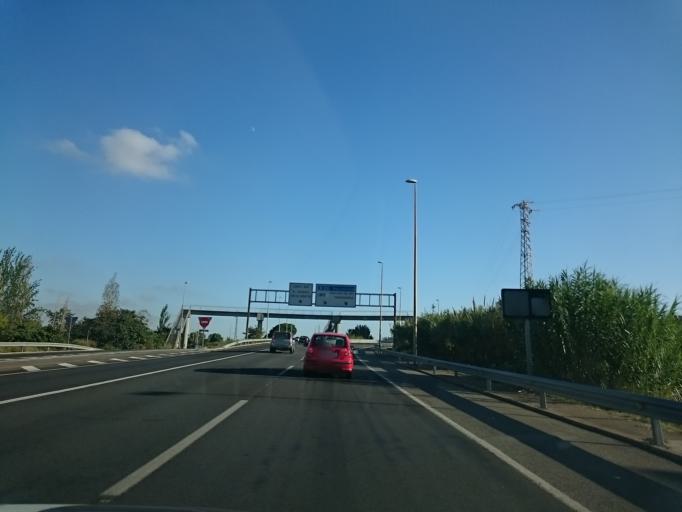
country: ES
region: Catalonia
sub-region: Provincia de Barcelona
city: Molins de Rei
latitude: 41.4089
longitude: 2.0029
